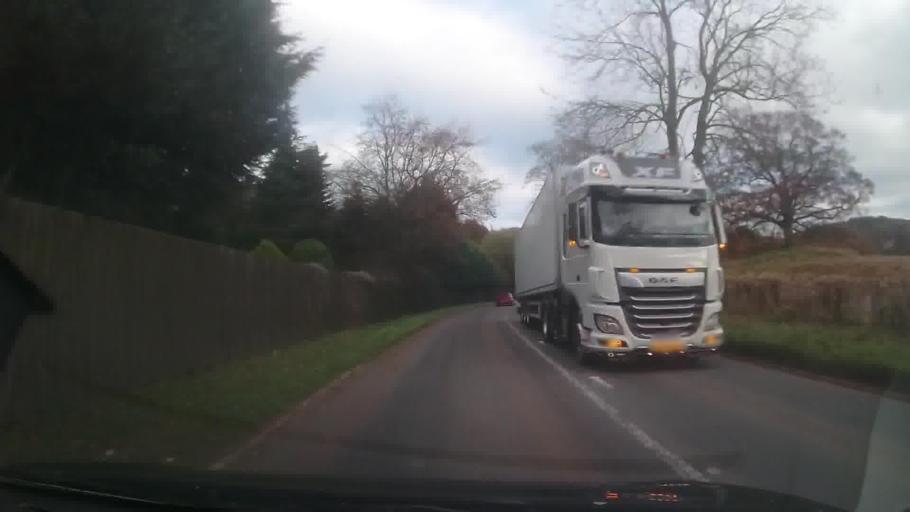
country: GB
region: England
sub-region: Staffordshire
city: Standon
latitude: 52.9498
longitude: -2.3283
